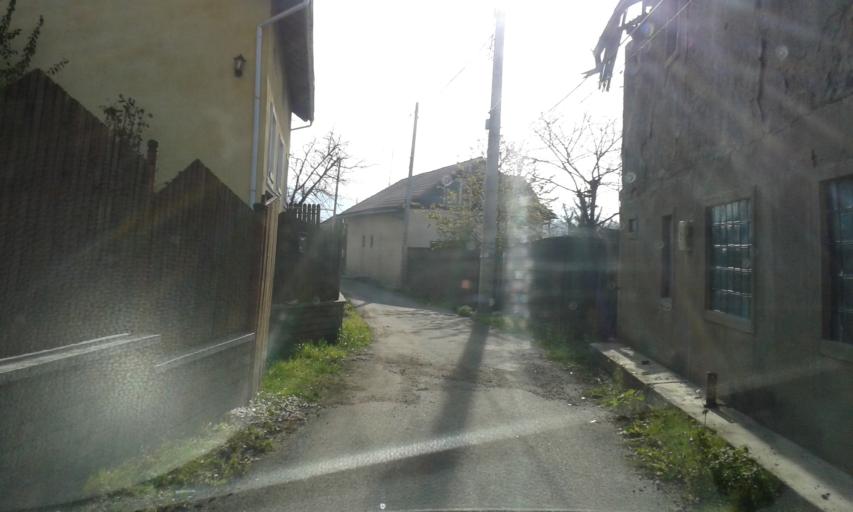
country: RO
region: Hunedoara
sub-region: Municipiul Petrosani
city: Petrosani
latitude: 45.4201
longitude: 23.3745
